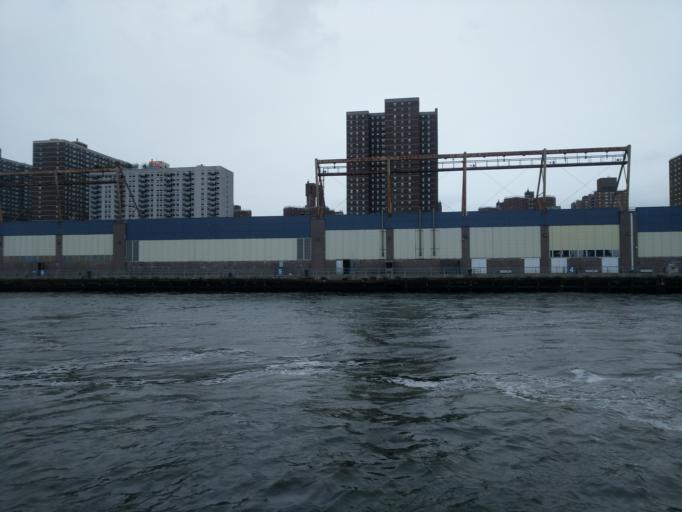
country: US
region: New York
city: New York City
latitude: 40.7089
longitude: -73.9857
